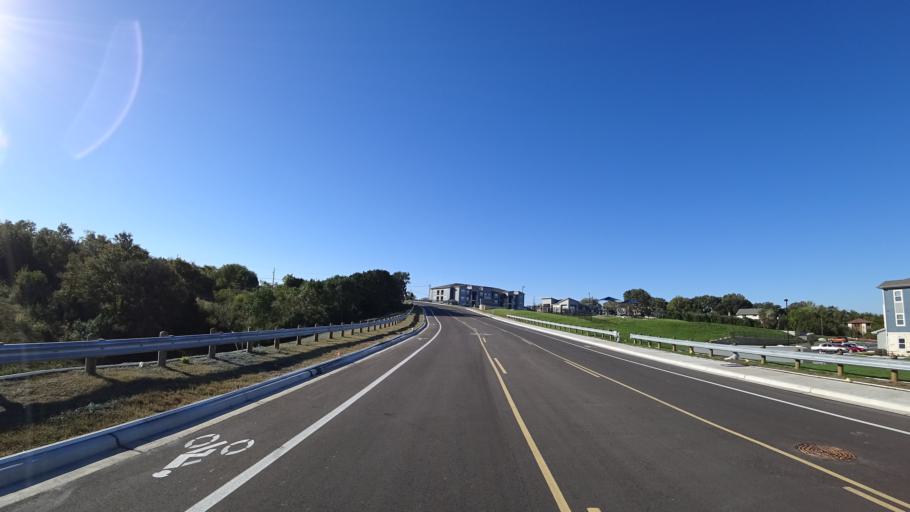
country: US
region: Texas
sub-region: Travis County
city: Manor
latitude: 30.3282
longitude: -97.6380
